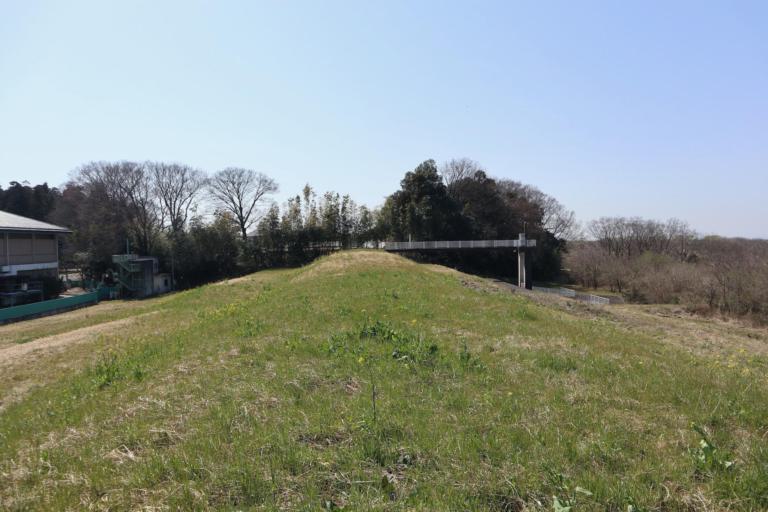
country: JP
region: Ibaraki
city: Koga
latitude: 36.2120
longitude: 139.6989
